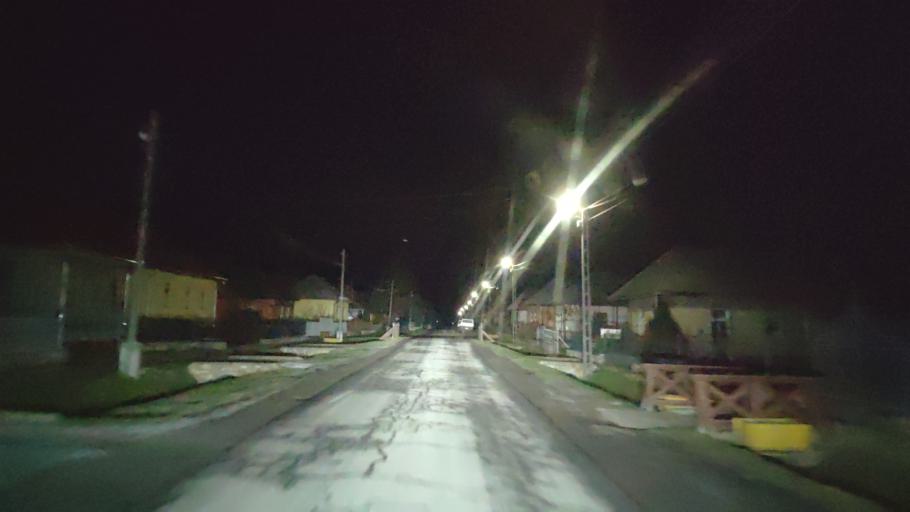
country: HU
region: Borsod-Abauj-Zemplen
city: Satoraljaujhely
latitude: 48.4662
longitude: 21.6175
